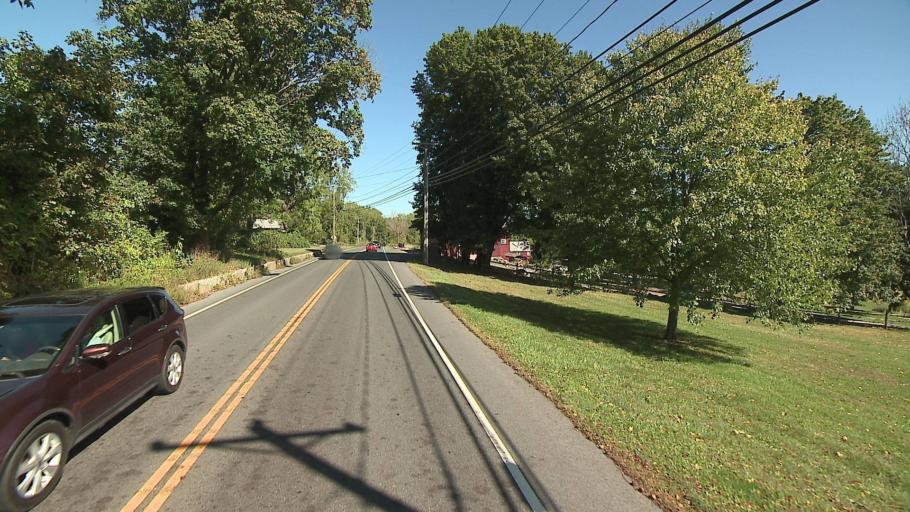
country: US
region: Connecticut
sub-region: Litchfield County
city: New Milford
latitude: 41.6087
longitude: -73.4031
